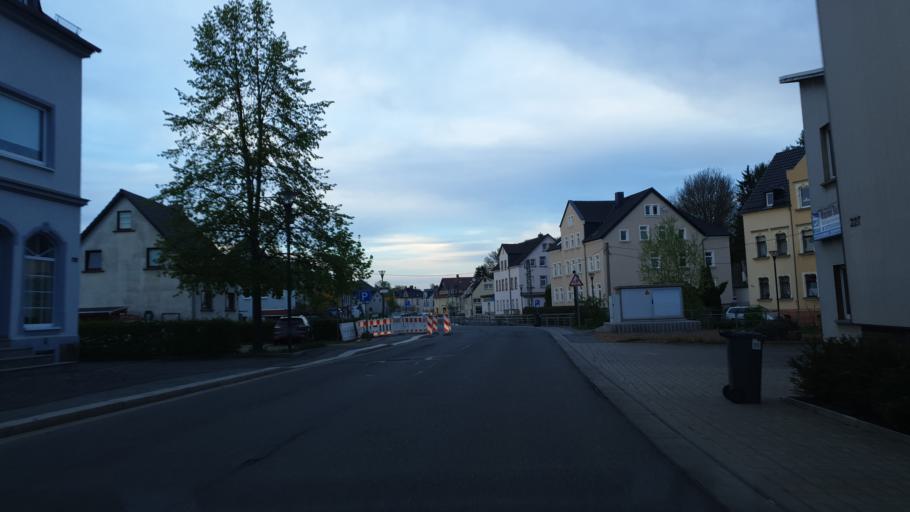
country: DE
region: Saxony
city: Gersdorf
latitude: 50.7568
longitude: 12.7079
